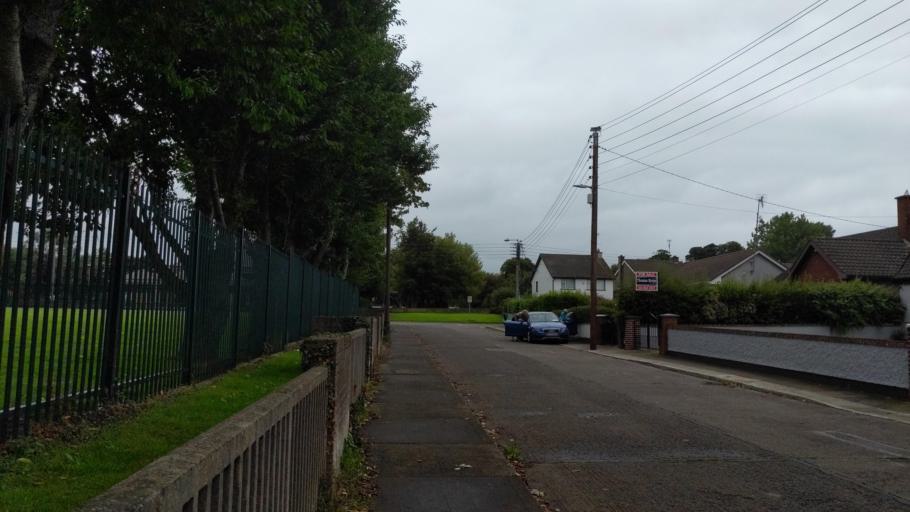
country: IE
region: Leinster
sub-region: Lu
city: Drogheda
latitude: 53.7112
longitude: -6.3590
